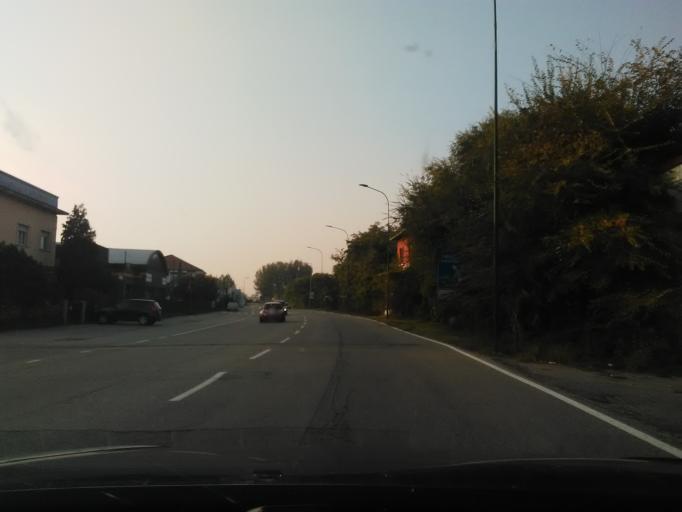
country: IT
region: Piedmont
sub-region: Provincia di Alessandria
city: Casale Monferrato
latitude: 45.1507
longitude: 8.4426
